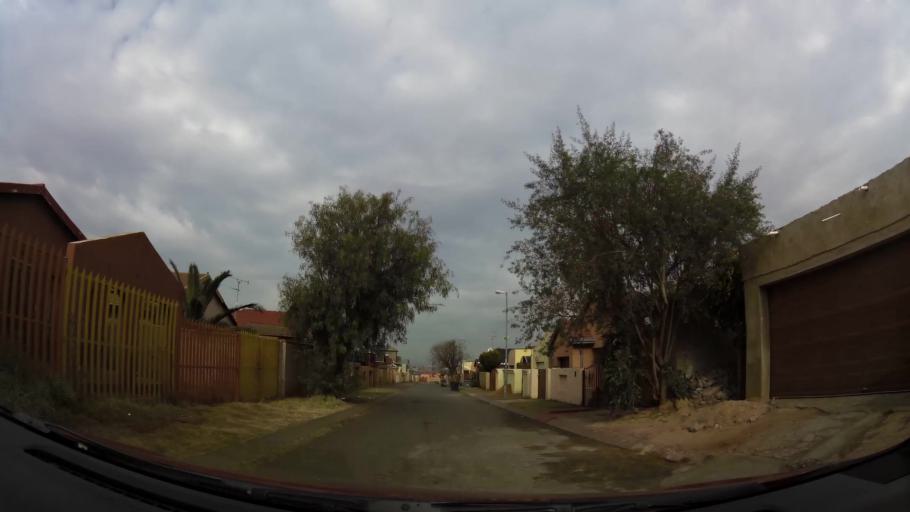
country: ZA
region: Gauteng
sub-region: City of Johannesburg Metropolitan Municipality
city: Soweto
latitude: -26.2767
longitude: 27.8357
